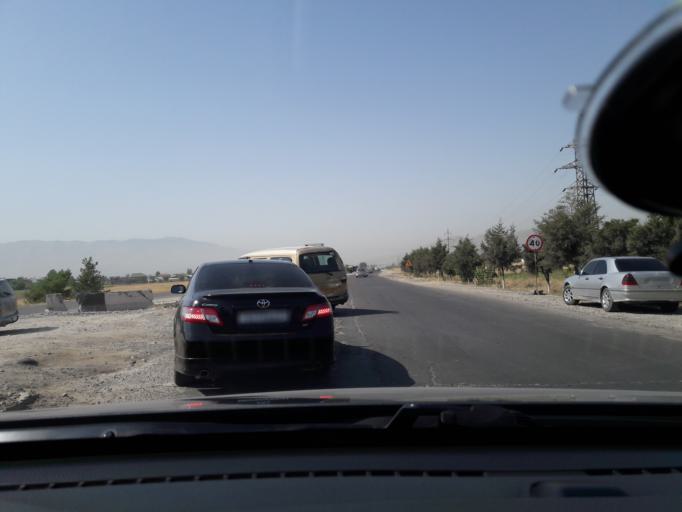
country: TJ
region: Dushanbe
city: Dushanbe
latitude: 38.4985
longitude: 68.7552
